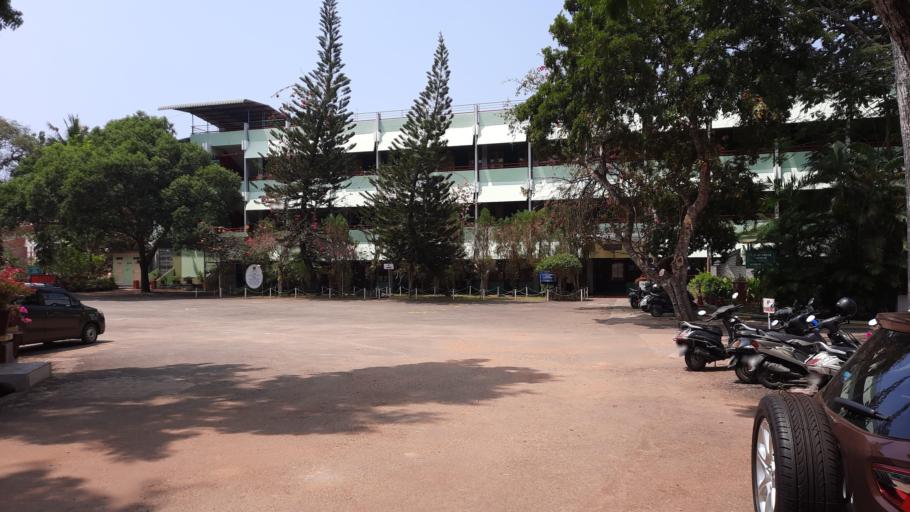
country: IN
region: Kerala
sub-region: Thiruvananthapuram
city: Thiruvananthapuram
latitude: 8.5424
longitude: 76.9121
